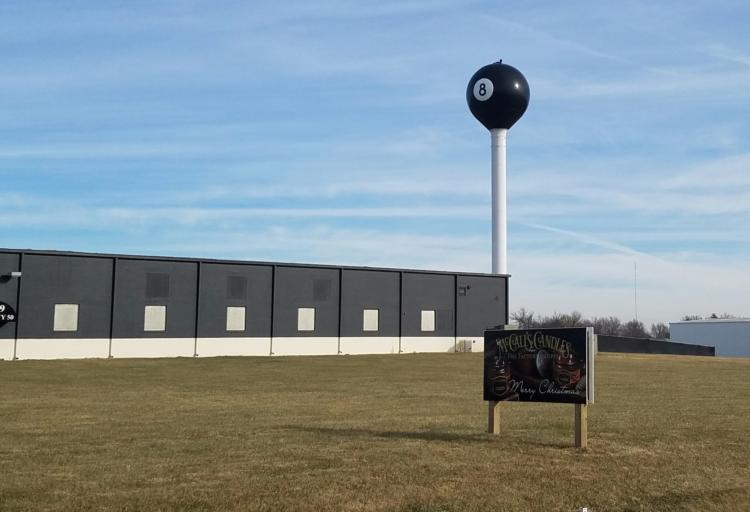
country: US
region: Missouri
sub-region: Moniteau County
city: Tipton
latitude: 38.6537
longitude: -92.7980
